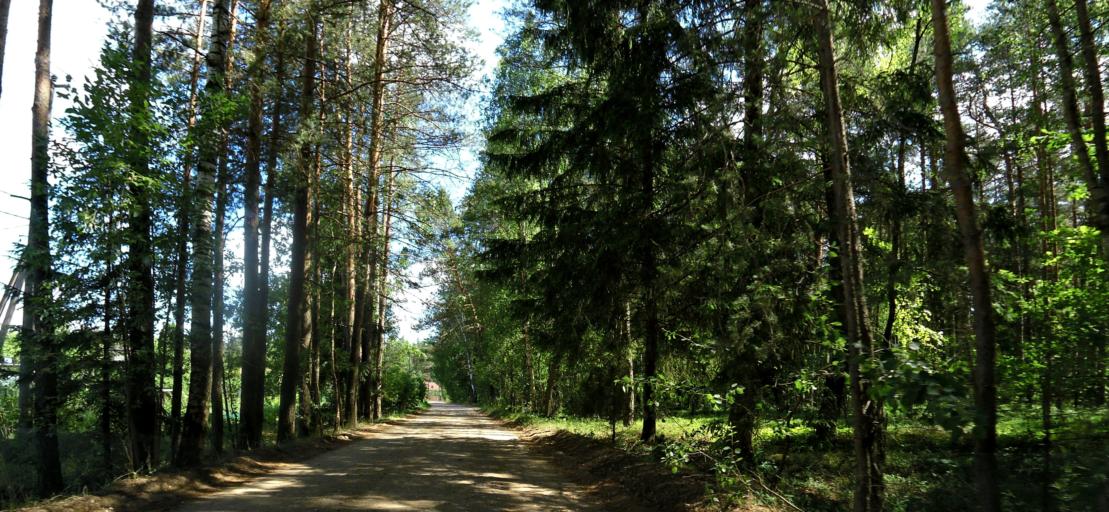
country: LT
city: Nemencine
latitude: 54.8239
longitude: 25.4102
